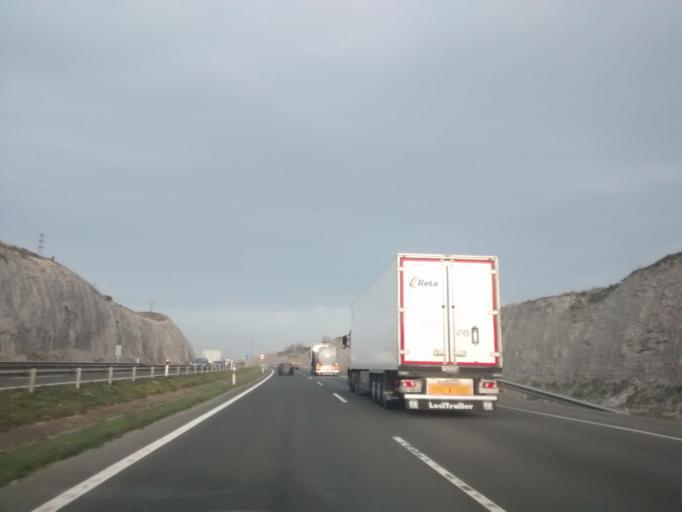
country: ES
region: Basque Country
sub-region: Provincia de Alava
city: Gasteiz / Vitoria
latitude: 42.8286
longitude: -2.7599
